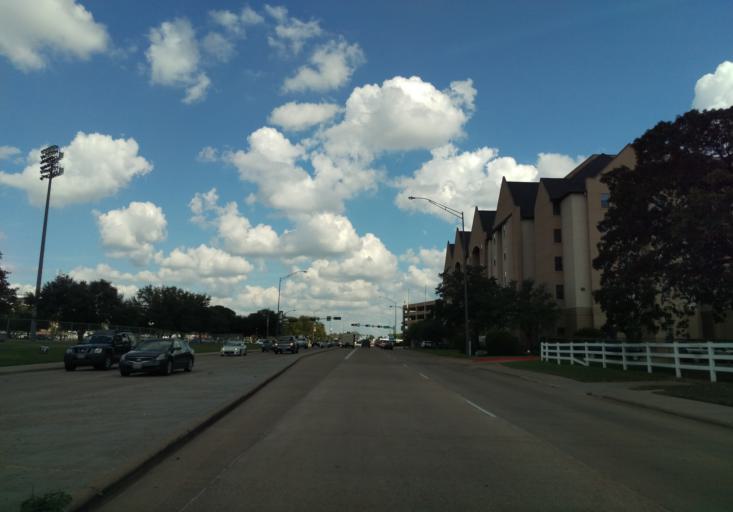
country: US
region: Texas
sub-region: Brazos County
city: College Station
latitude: 30.6020
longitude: -96.3423
